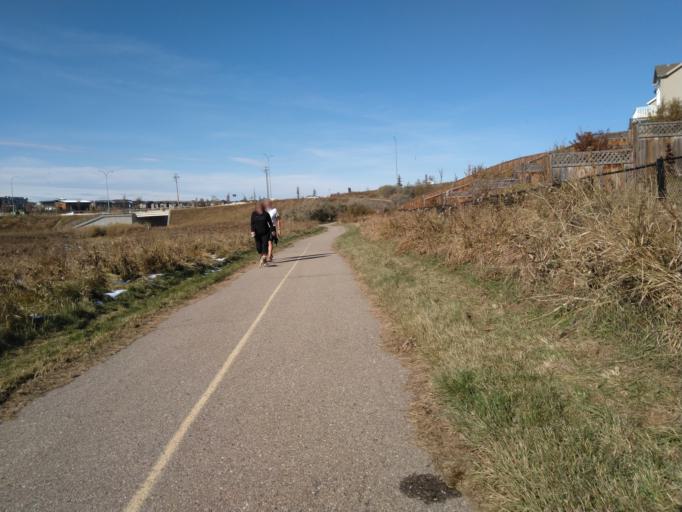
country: CA
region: Alberta
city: Calgary
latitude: 51.1668
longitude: -114.1259
